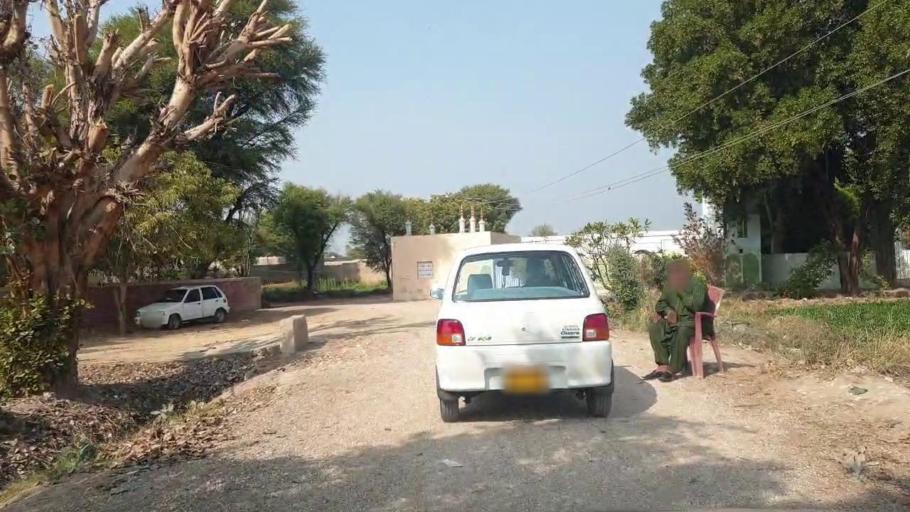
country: PK
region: Sindh
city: Hala
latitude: 25.8273
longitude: 68.4317
